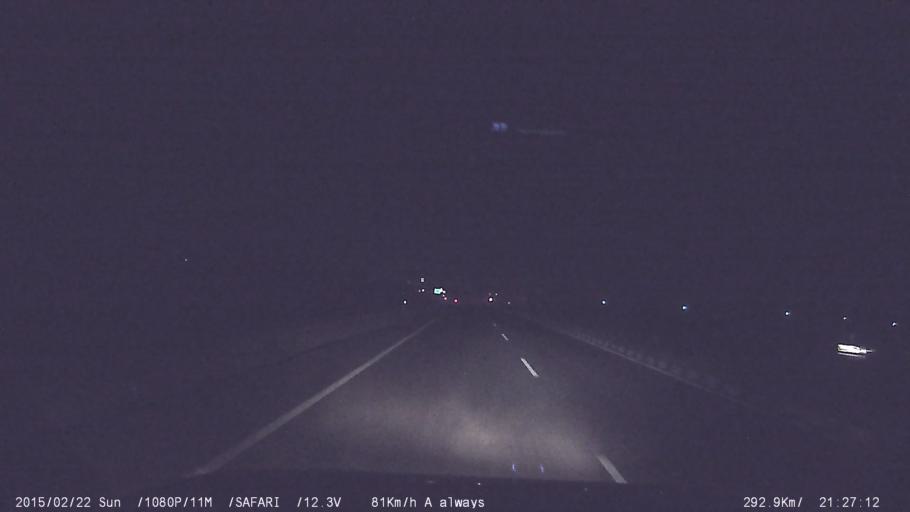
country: IN
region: Tamil Nadu
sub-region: Karur
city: Karur
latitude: 10.9132
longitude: 78.0414
